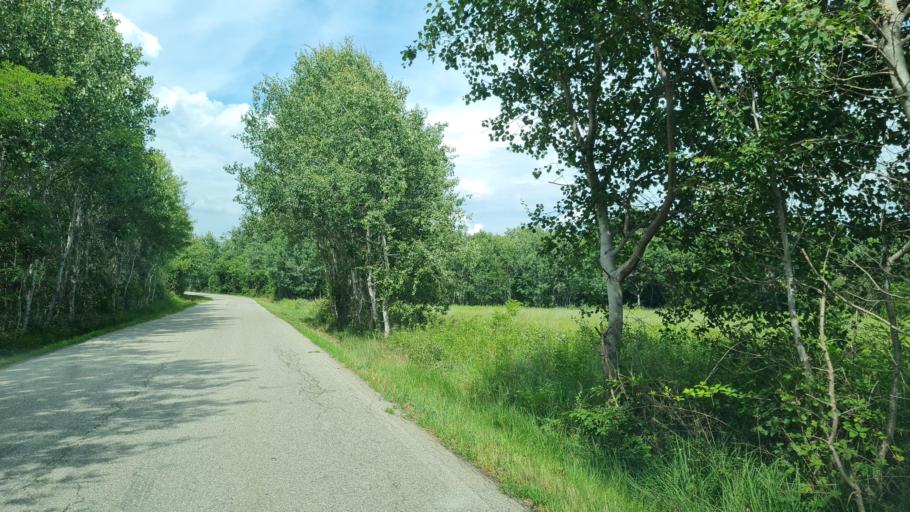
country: IT
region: Piedmont
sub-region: Provincia di Biella
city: Castelletto Cervo
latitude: 45.5463
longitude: 8.2259
